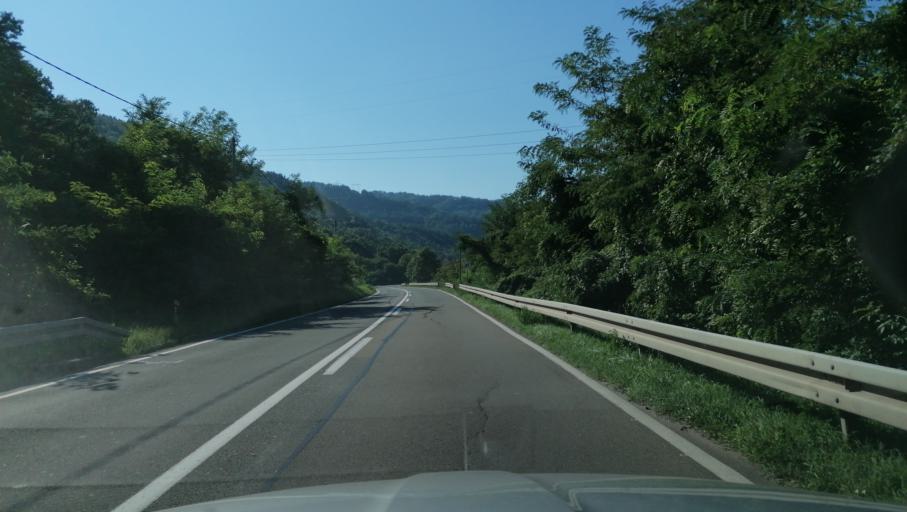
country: RS
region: Central Serbia
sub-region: Raski Okrug
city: Kraljevo
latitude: 43.6683
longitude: 20.5842
